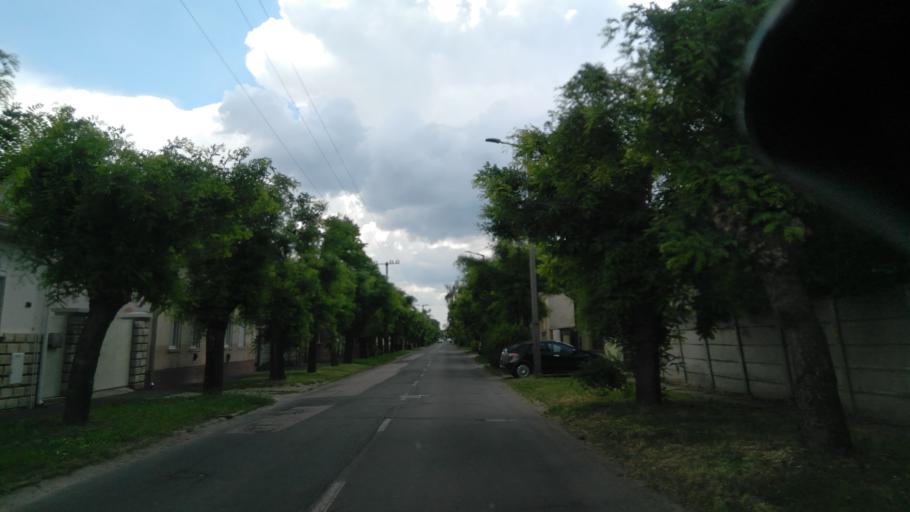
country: HU
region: Bekes
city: Gyula
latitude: 46.6539
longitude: 21.2697
